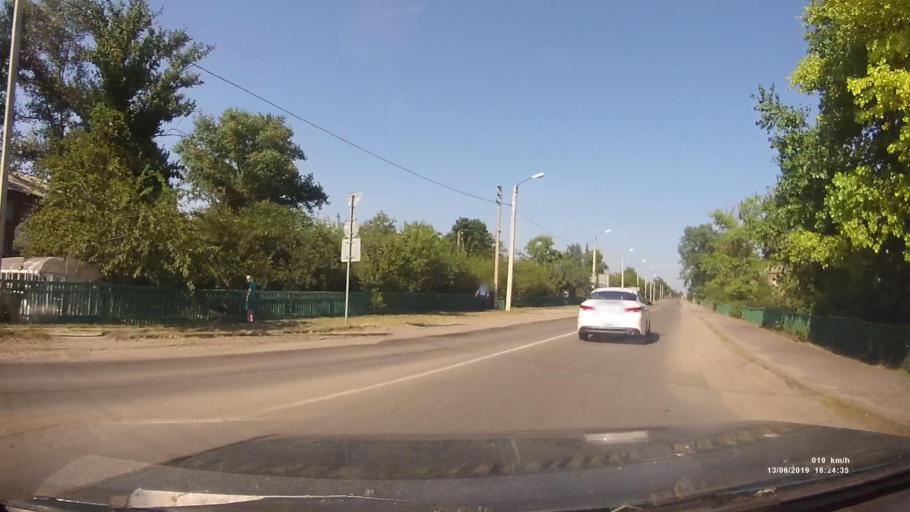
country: RU
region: Rostov
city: Kazanskaya
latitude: 49.7982
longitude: 41.1454
